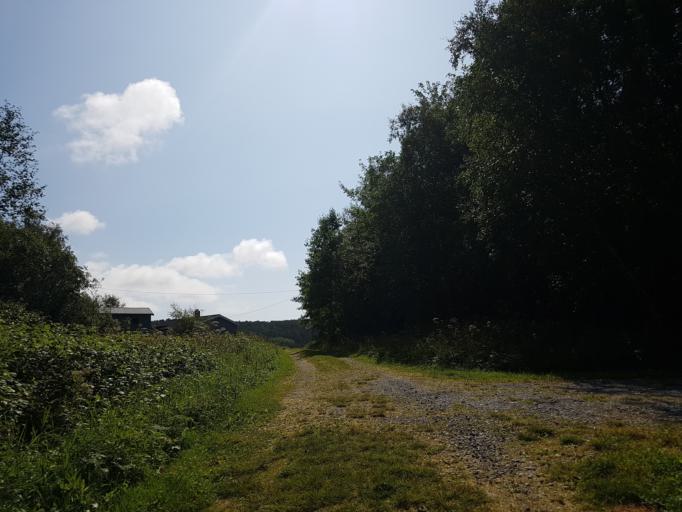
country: NO
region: Sor-Trondelag
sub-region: Agdenes
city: Lensvik
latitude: 63.6336
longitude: 9.8411
